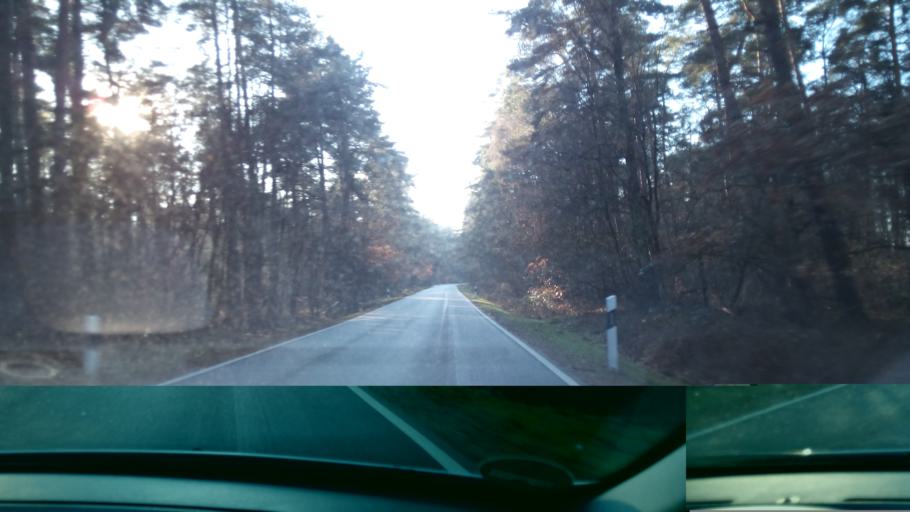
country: DE
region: Schleswig-Holstein
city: Gottin
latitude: 53.5140
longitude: 10.6964
